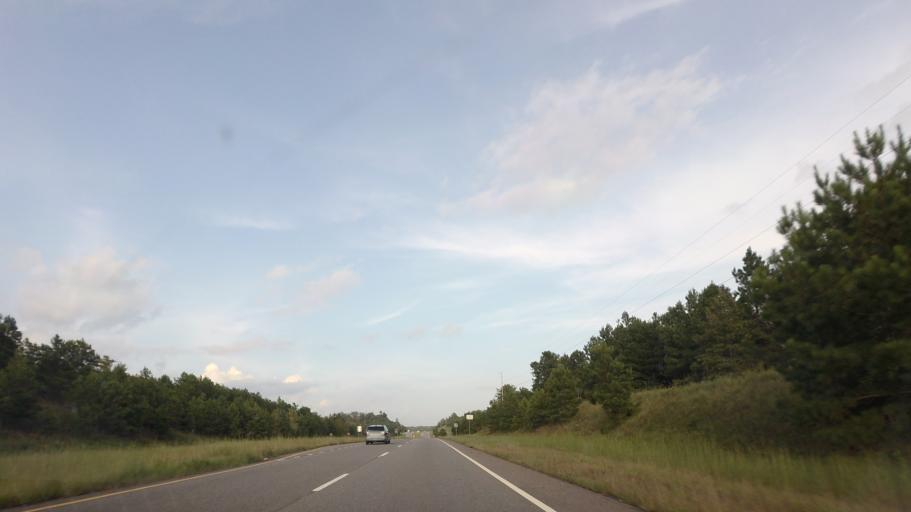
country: US
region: Georgia
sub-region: Wilkinson County
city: Gordon
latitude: 32.8523
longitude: -83.4026
